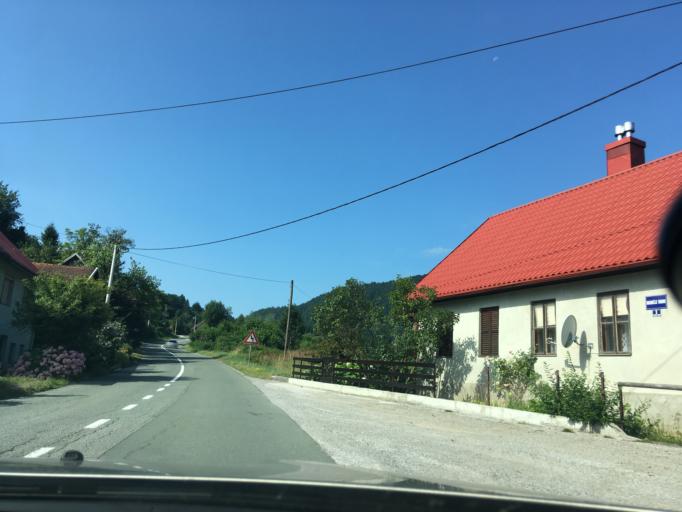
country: HR
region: Primorsko-Goranska
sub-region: Grad Delnice
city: Delnice
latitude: 45.4220
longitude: 14.8260
